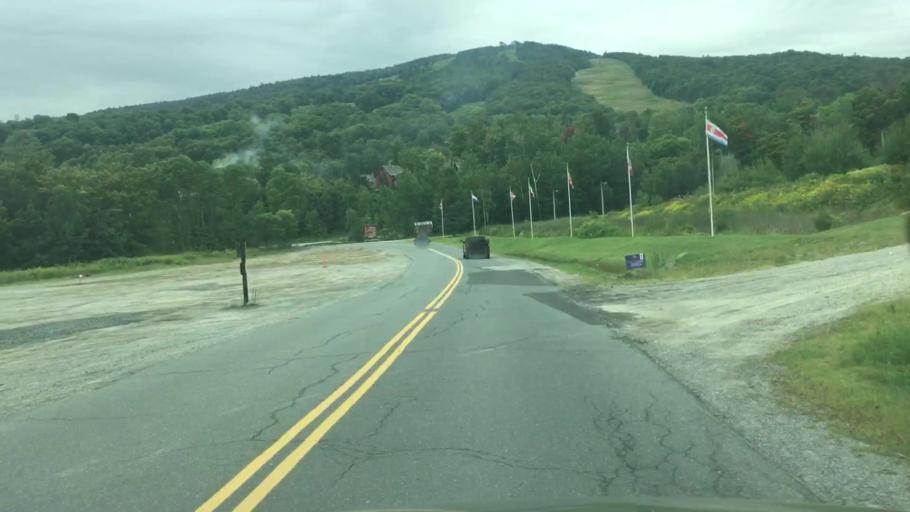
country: US
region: Vermont
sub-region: Windham County
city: Dover
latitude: 42.9722
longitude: -72.8957
